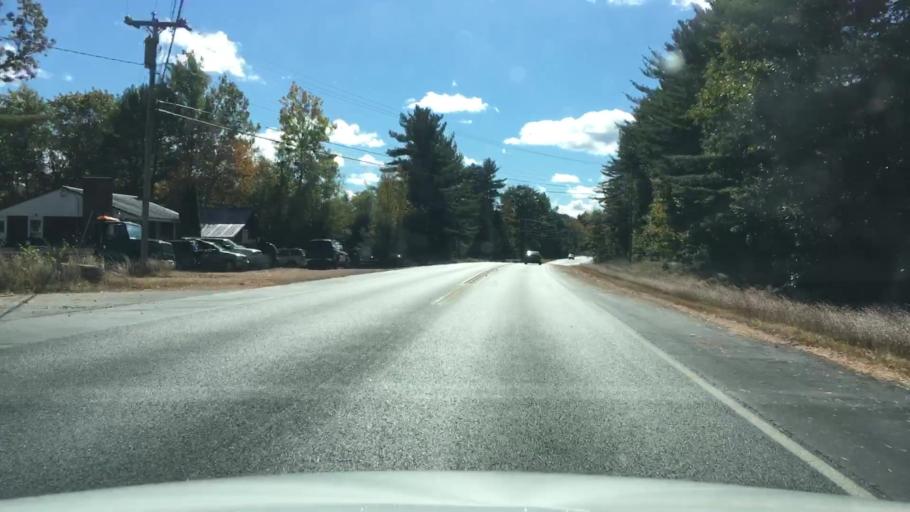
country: US
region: Maine
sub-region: York County
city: Alfred
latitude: 43.4593
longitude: -70.7194
